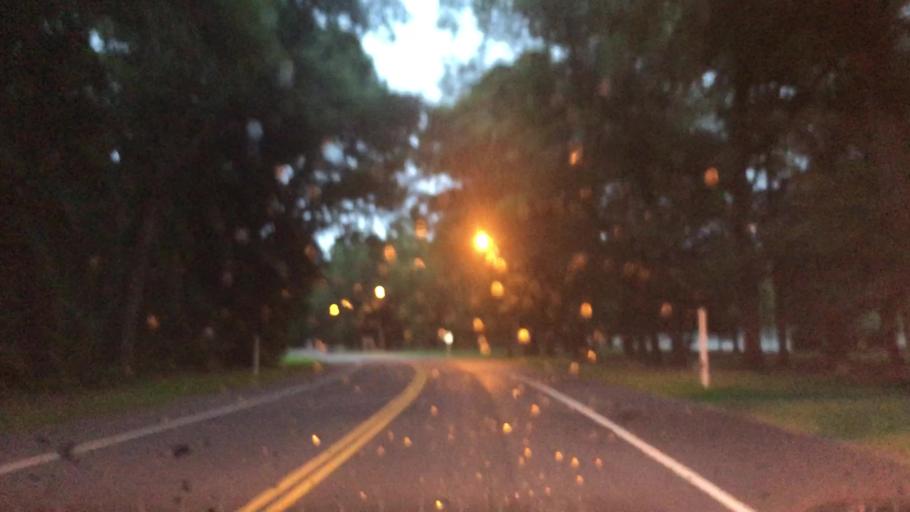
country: US
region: New York
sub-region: Nassau County
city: Lakeview
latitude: 40.6783
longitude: -73.6463
